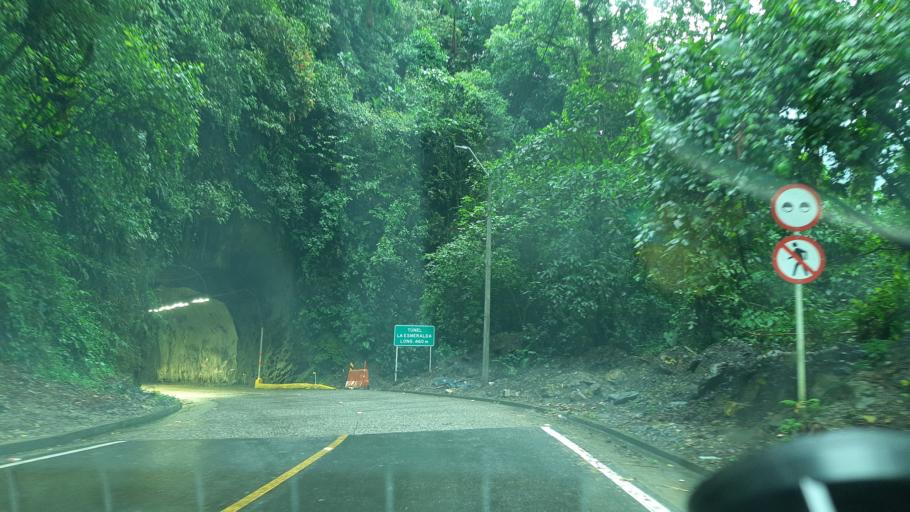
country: CO
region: Boyaca
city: Santa Maria
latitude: 4.9065
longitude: -73.2953
